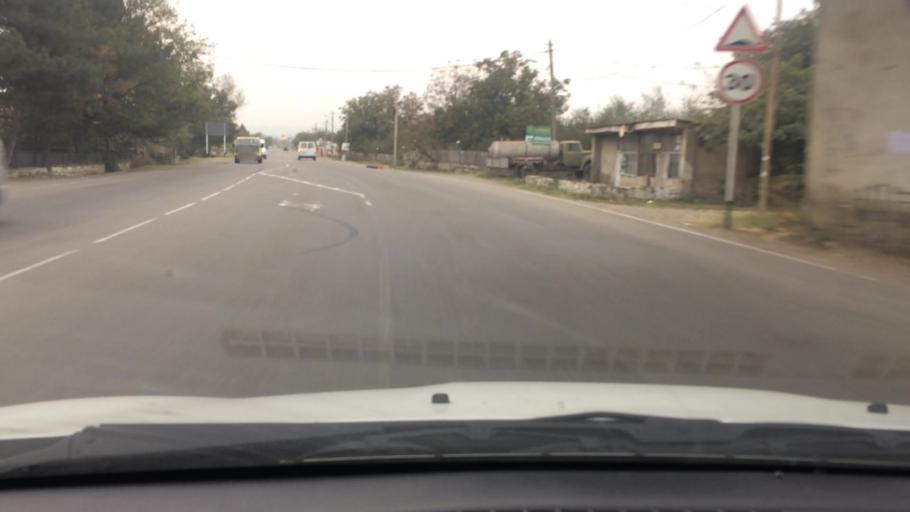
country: GE
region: Kvemo Kartli
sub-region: Marneuli
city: Marneuli
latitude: 41.5797
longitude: 44.7744
